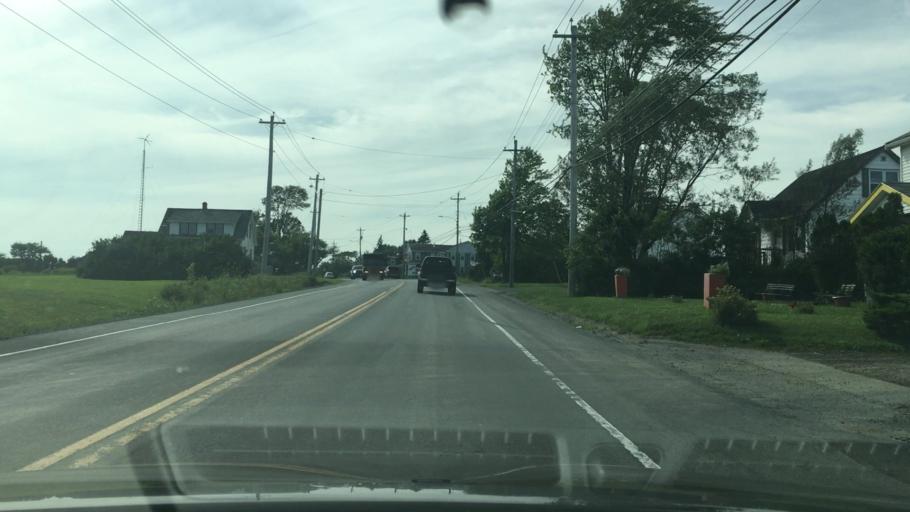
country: CA
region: Nova Scotia
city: Dartmouth
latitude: 44.7331
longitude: -63.7620
